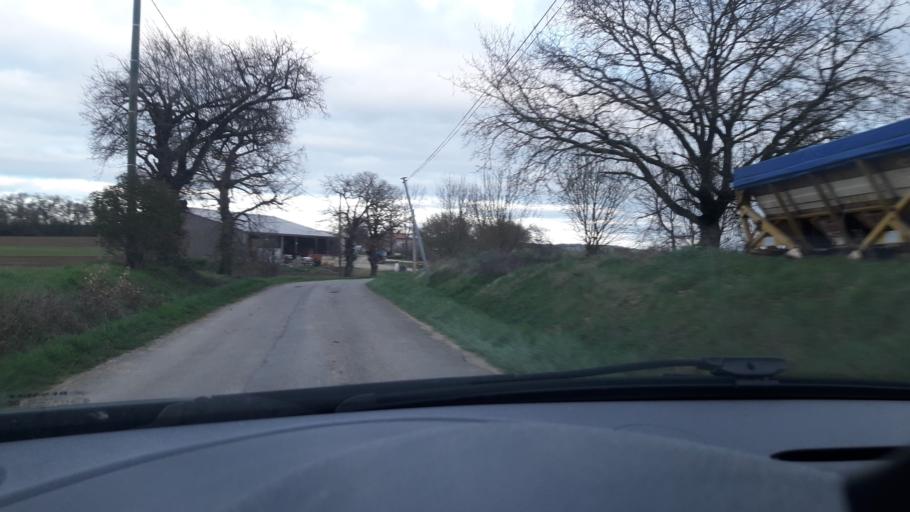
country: FR
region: Midi-Pyrenees
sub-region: Departement de la Haute-Garonne
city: Launac
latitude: 43.7010
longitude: 1.0586
